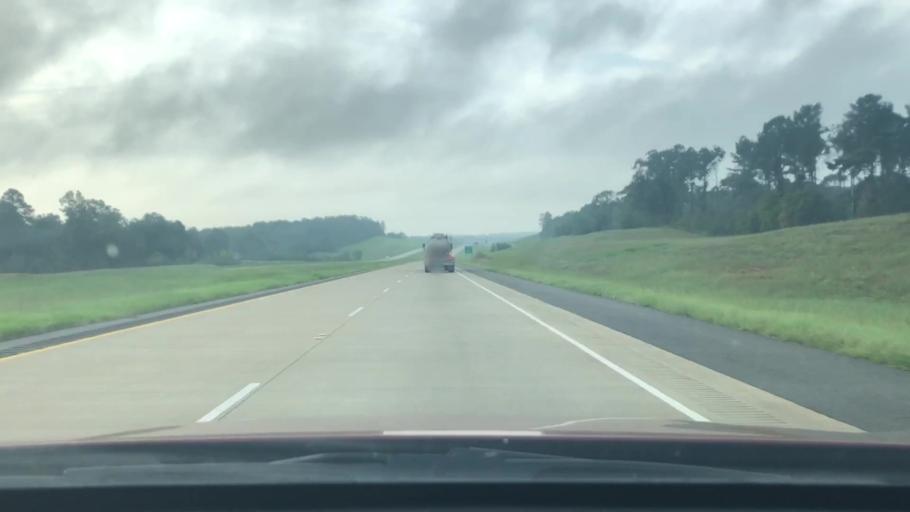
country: US
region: Louisiana
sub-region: Caddo Parish
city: Vivian
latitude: 32.9571
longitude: -93.9021
